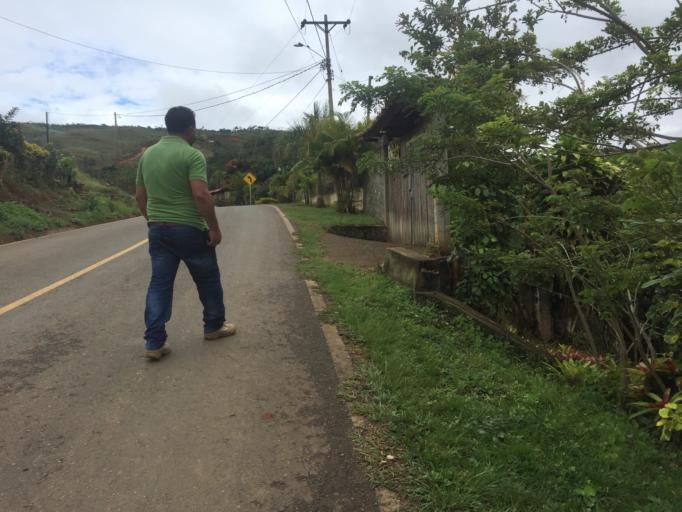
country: CO
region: Valle del Cauca
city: Dagua
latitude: 3.6871
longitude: -76.5927
